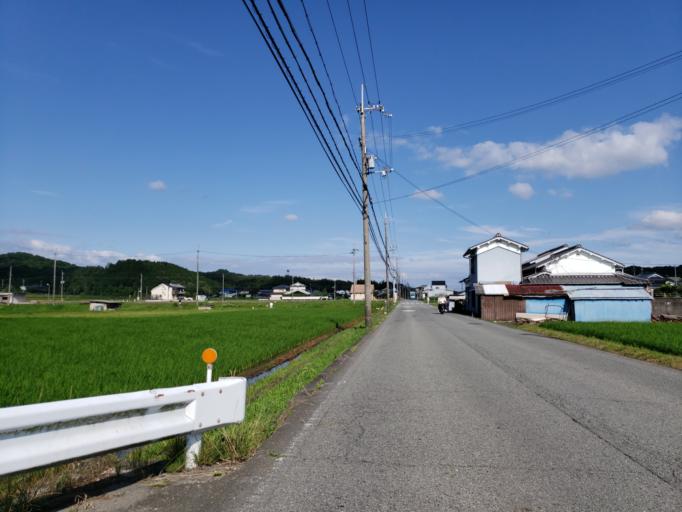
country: JP
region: Hyogo
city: Himeji
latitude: 34.9091
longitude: 134.7790
